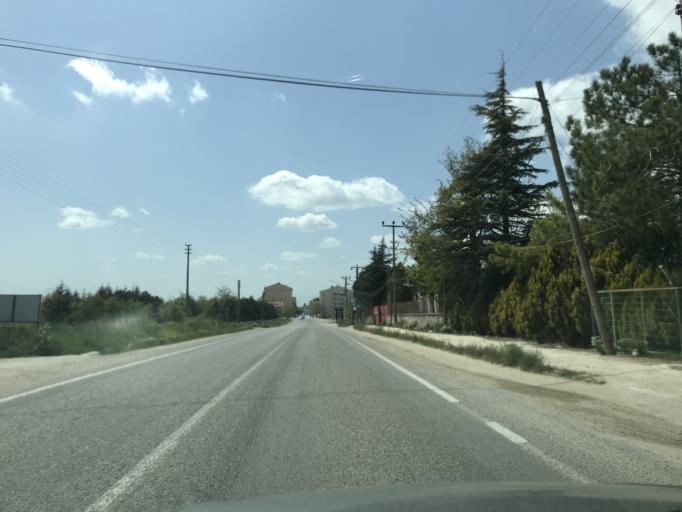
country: TR
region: Kirklareli
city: Pinarhisar
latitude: 41.6228
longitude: 27.5313
